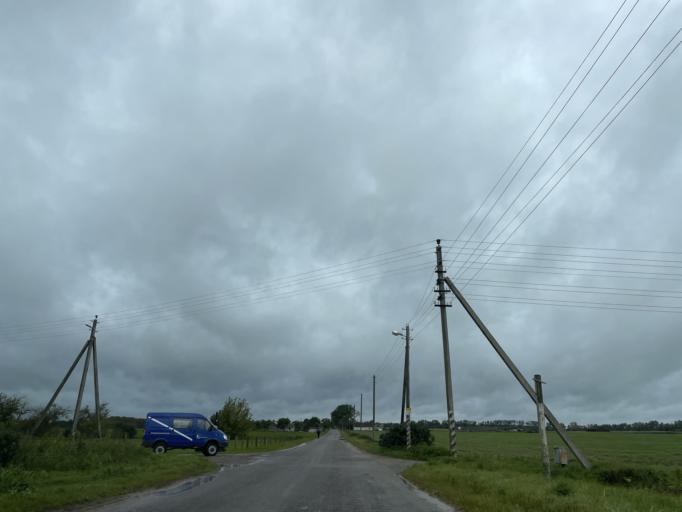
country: BY
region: Brest
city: Lyakhavichy
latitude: 53.1908
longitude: 26.2496
